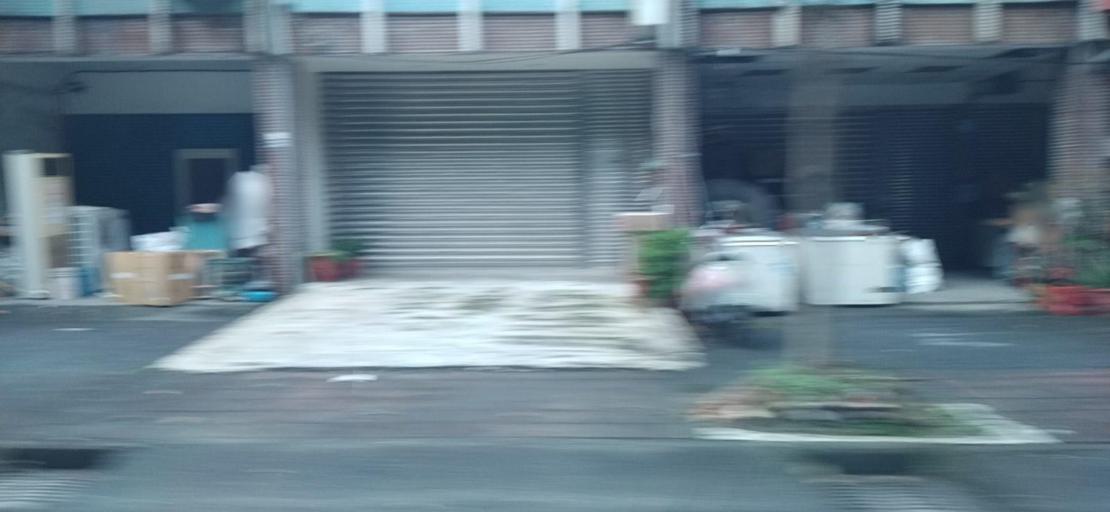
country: TW
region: Taiwan
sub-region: Yilan
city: Yilan
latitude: 24.6048
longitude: 121.8371
